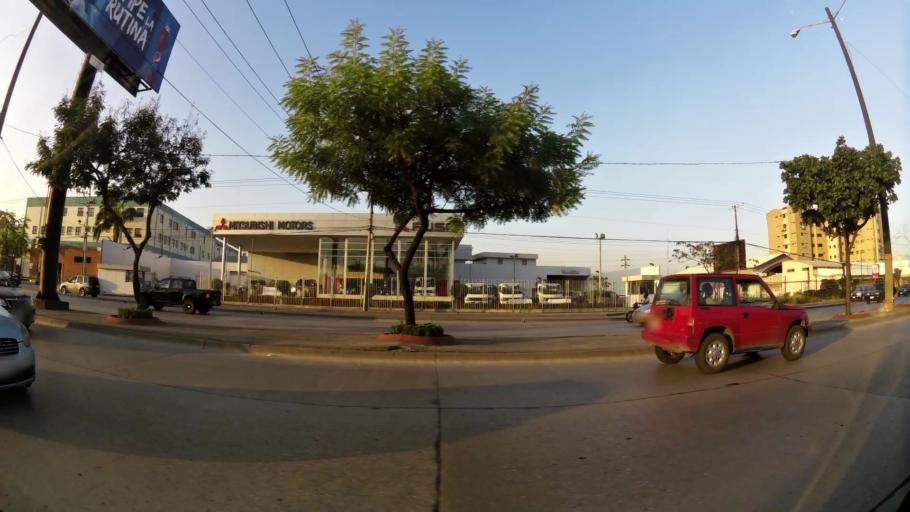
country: EC
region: Guayas
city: Eloy Alfaro
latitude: -2.1512
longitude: -79.8988
